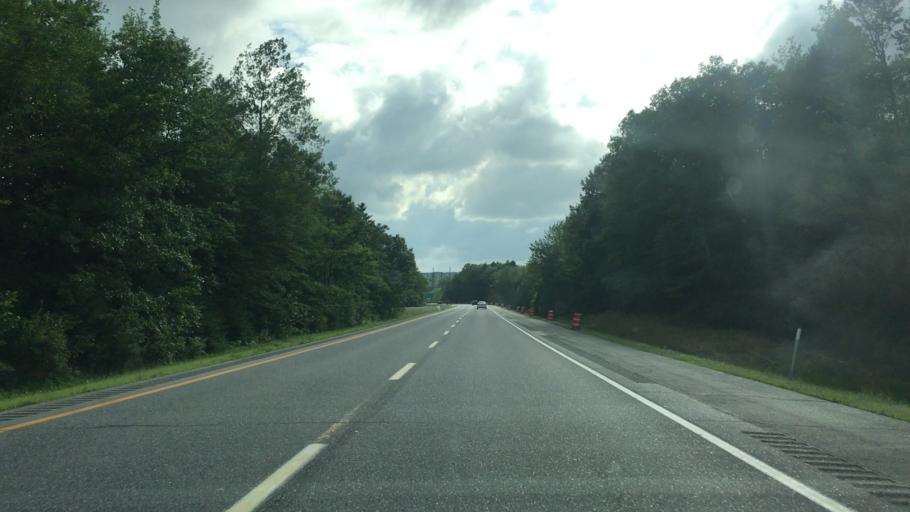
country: US
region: Maine
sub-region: Somerset County
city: Pittsfield
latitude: 44.8039
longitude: -69.3832
